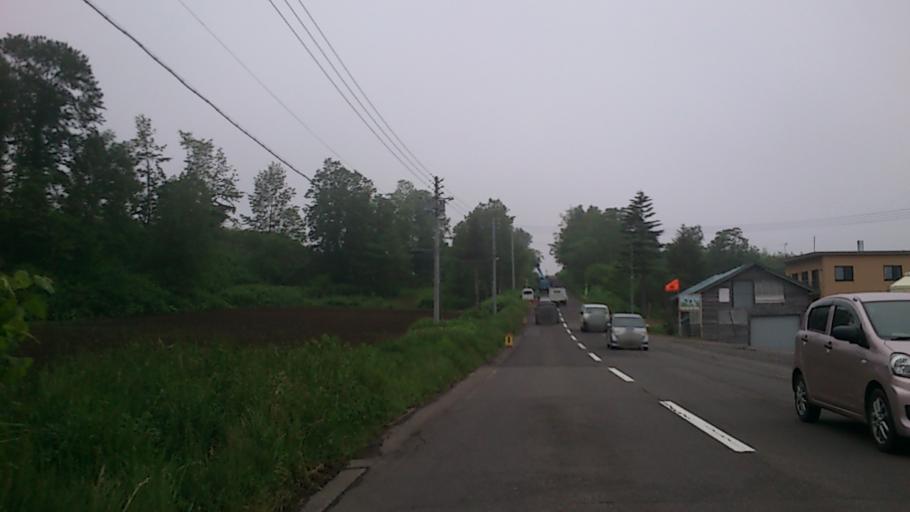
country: JP
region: Hokkaido
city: Niseko Town
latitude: 42.8802
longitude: 140.8294
